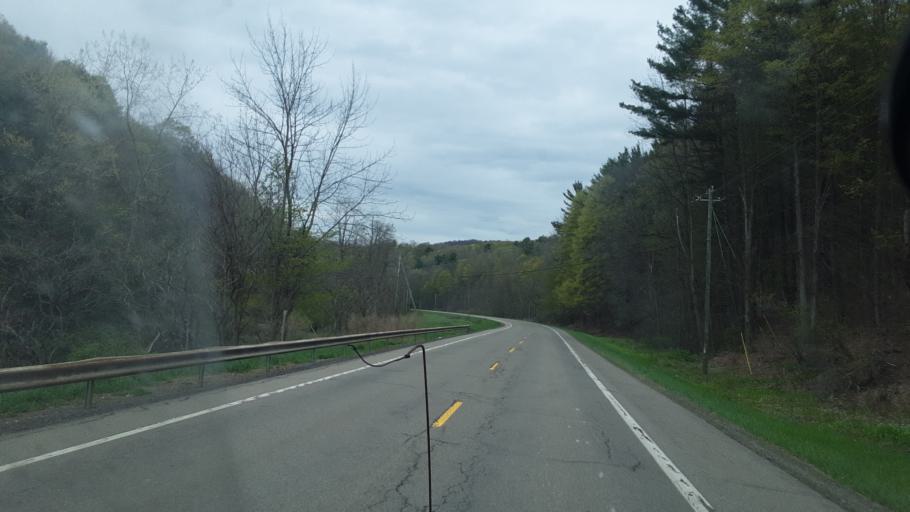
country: US
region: New York
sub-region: Steuben County
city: Canisteo
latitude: 42.1832
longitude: -77.5360
